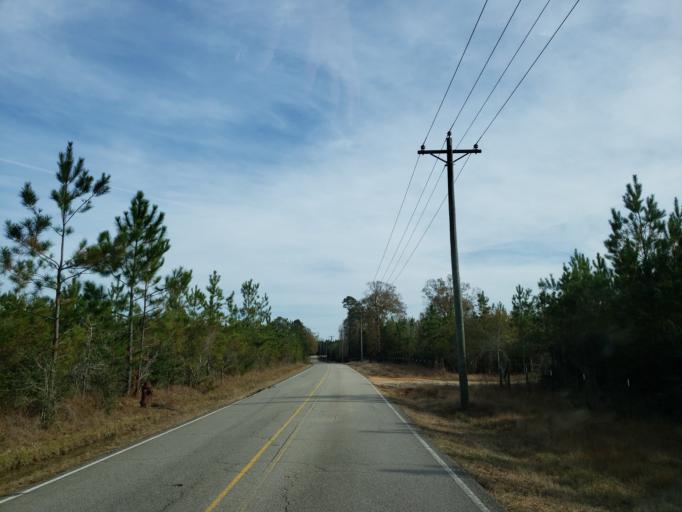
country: US
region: Mississippi
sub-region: Forrest County
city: Rawls Springs
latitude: 31.4172
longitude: -89.4211
